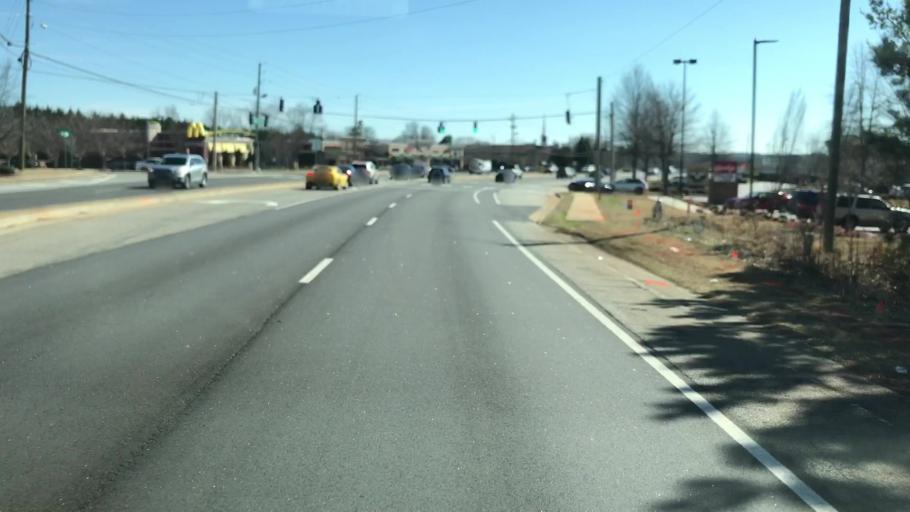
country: US
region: Georgia
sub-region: Gwinnett County
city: Lawrenceville
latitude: 33.9240
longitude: -84.0182
